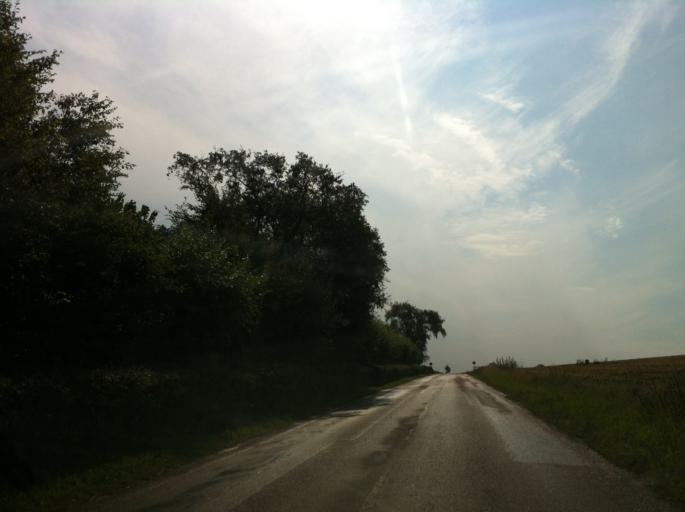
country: SE
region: Skane
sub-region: Helsingborg
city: Glumslov
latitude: 55.9298
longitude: 12.8742
